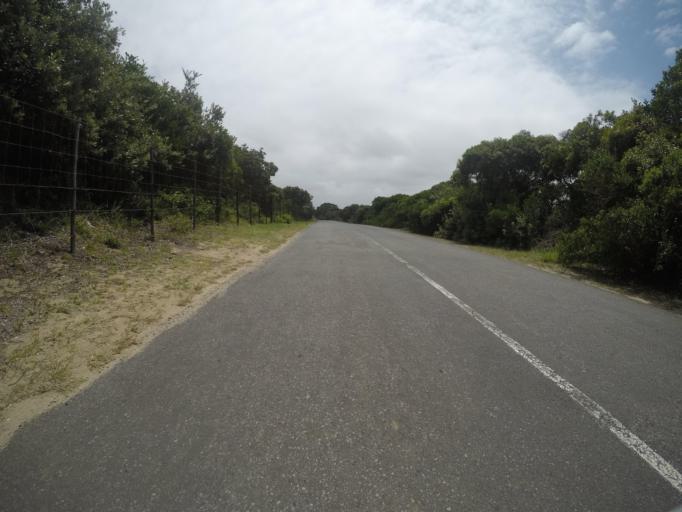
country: ZA
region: Eastern Cape
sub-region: Buffalo City Metropolitan Municipality
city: East London
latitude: -32.9946
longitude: 27.9468
